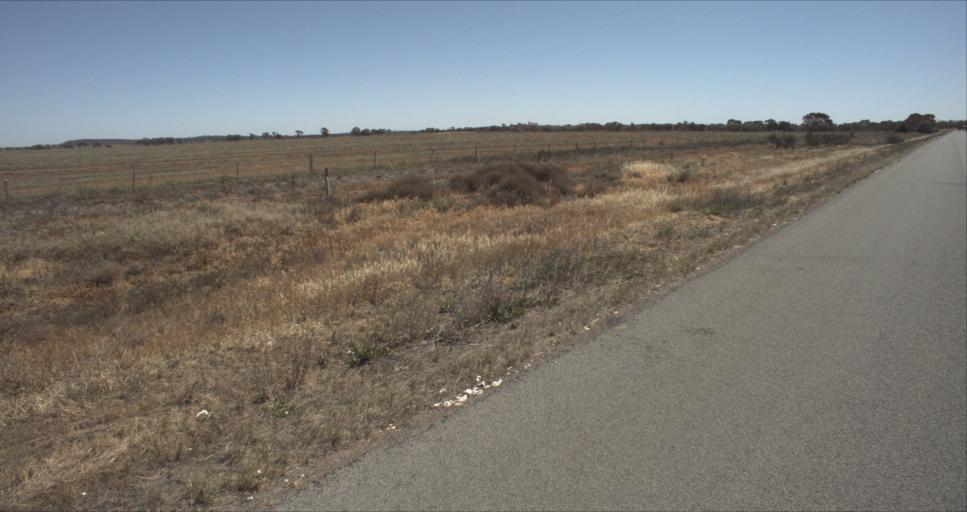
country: AU
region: New South Wales
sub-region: Leeton
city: Leeton
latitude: -34.4353
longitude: 146.2988
